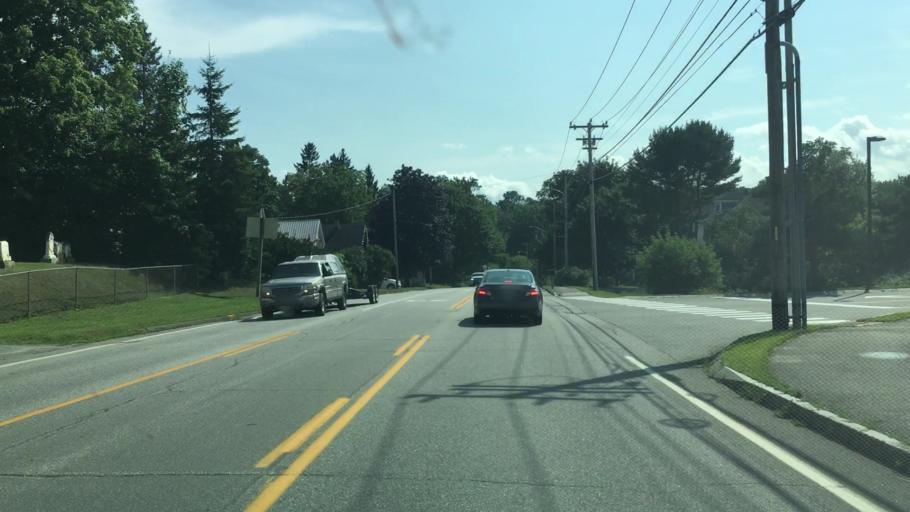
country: US
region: Maine
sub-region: Penobscot County
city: Hampden
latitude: 44.7381
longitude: -68.8396
